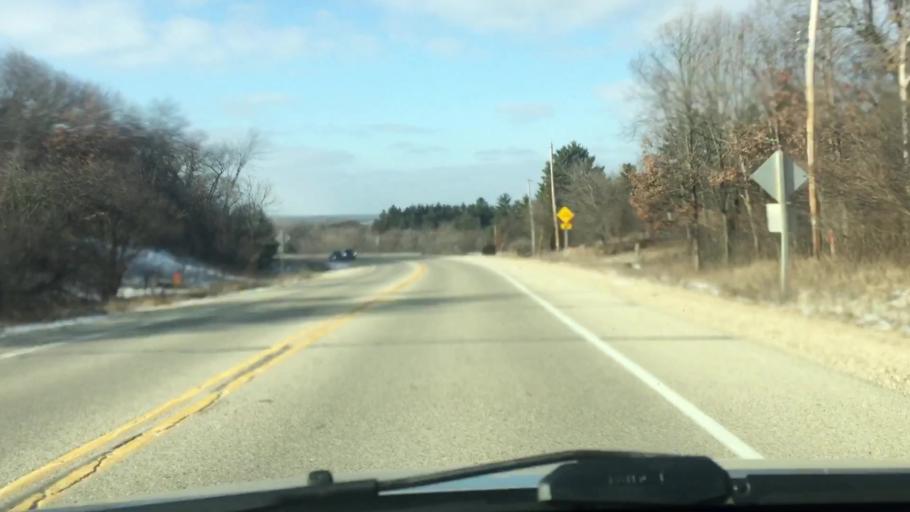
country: US
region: Wisconsin
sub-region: Waukesha County
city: Eagle
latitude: 42.8810
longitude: -88.4870
